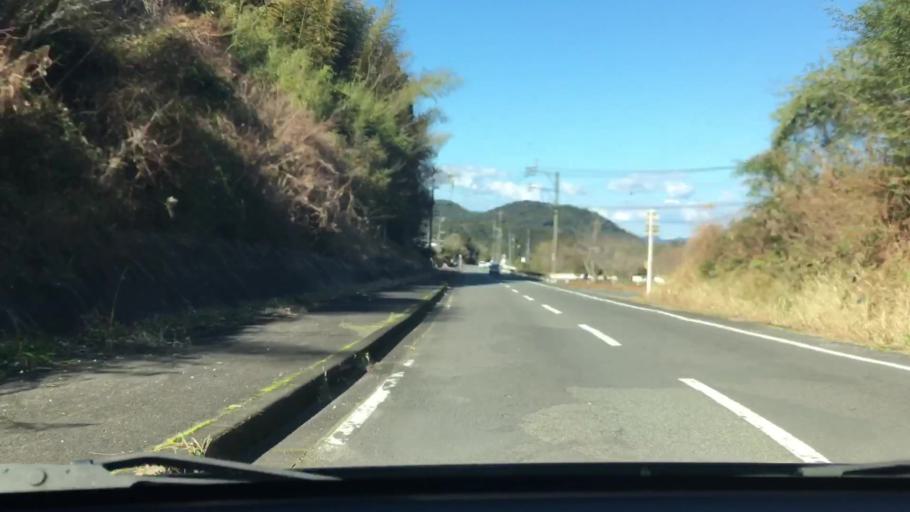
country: JP
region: Kagoshima
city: Satsumasendai
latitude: 31.7697
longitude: 130.4017
